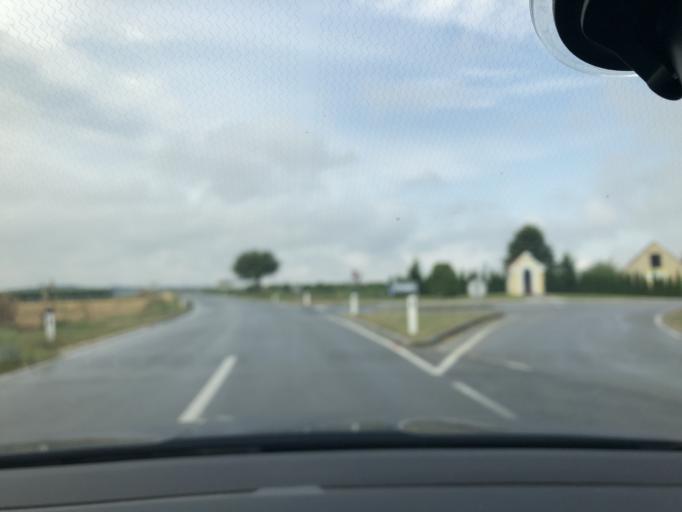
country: AT
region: Lower Austria
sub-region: Politischer Bezirk Mistelbach
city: Hochleithen
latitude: 48.4953
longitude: 16.5535
